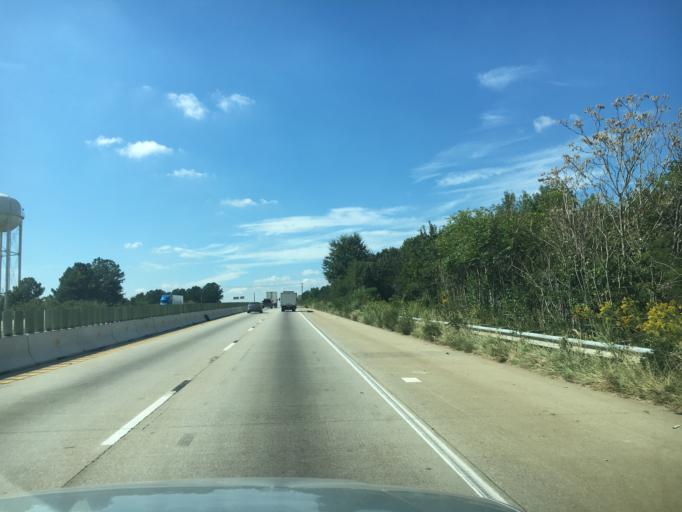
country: US
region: South Carolina
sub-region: Spartanburg County
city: Fairforest
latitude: 34.9699
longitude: -82.0263
